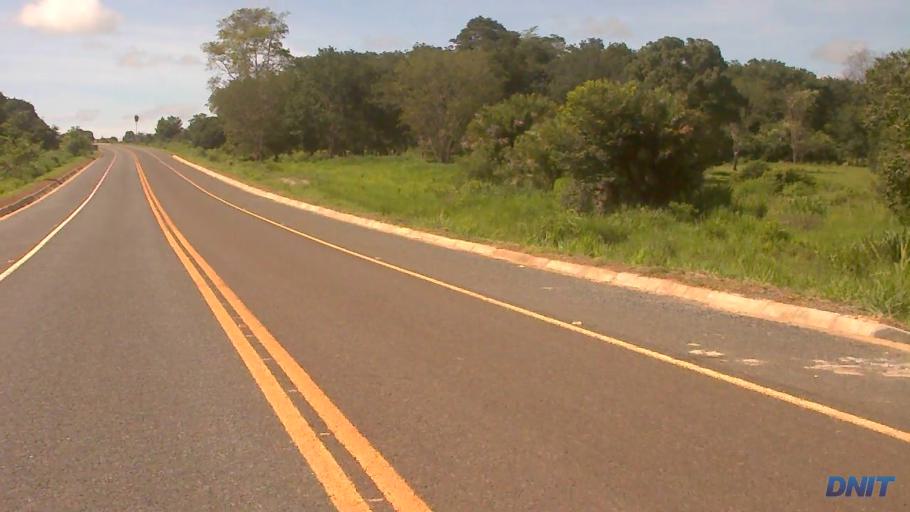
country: BR
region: Goias
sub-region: Sao Miguel Do Araguaia
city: Sao Miguel do Araguaia
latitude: -13.2922
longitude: -50.1774
